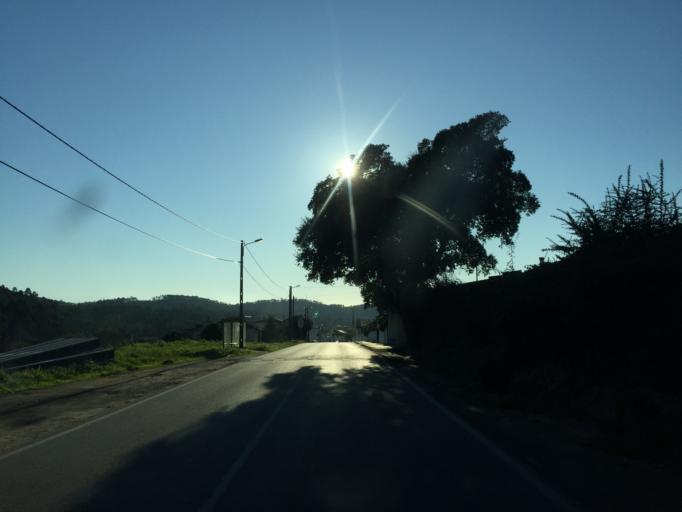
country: PT
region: Coimbra
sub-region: Figueira da Foz
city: Alhadas
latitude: 40.1671
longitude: -8.8073
